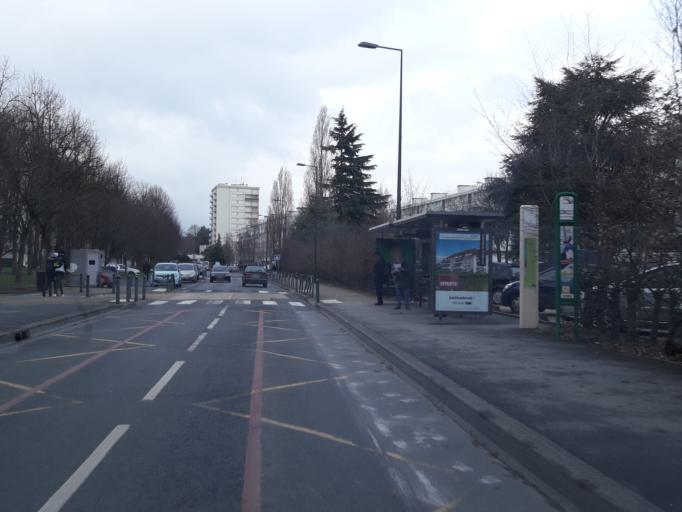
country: FR
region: Ile-de-France
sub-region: Departement de l'Essonne
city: Sainte-Genevieve-des-Bois
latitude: 48.6342
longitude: 2.3230
